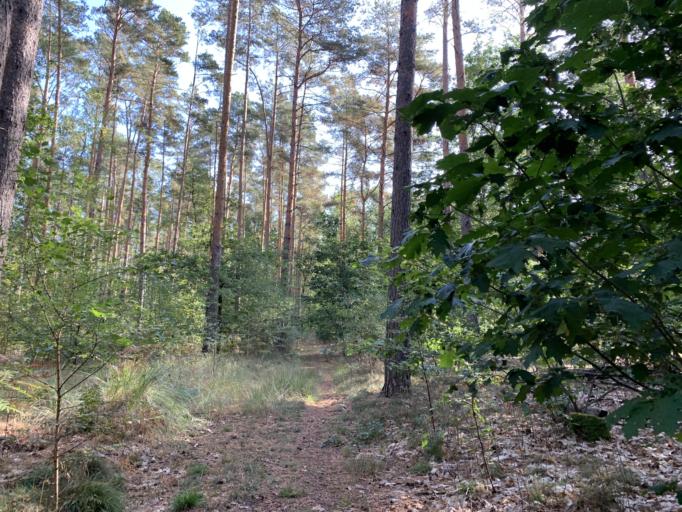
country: DE
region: Berlin
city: Wannsee
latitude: 52.4050
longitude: 13.1782
